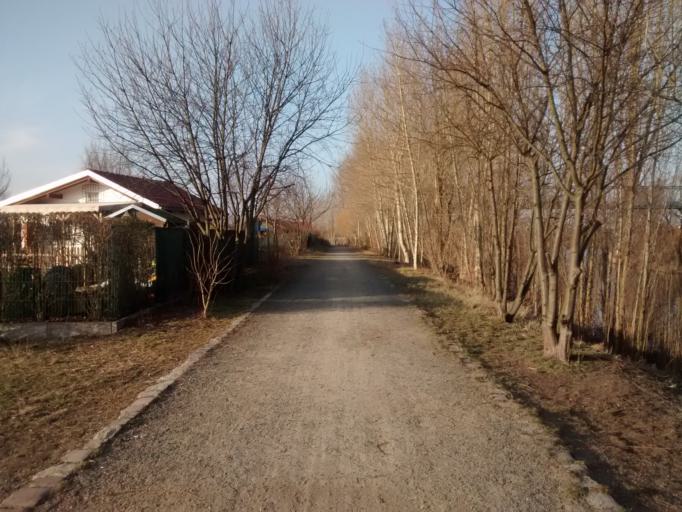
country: DE
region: Berlin
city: Charlottenburg-Nord
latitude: 52.5329
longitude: 13.3124
